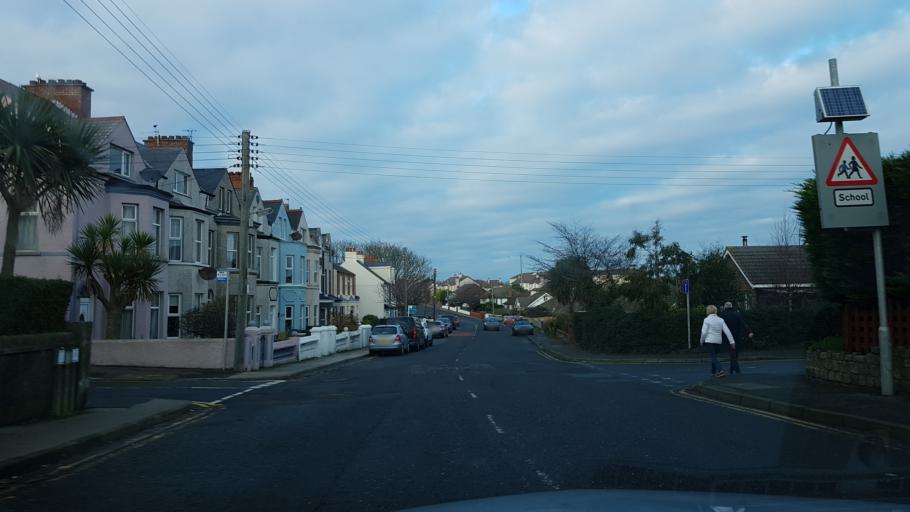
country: GB
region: Northern Ireland
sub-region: Down District
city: Donaghadee
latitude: 54.6375
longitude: -5.5331
